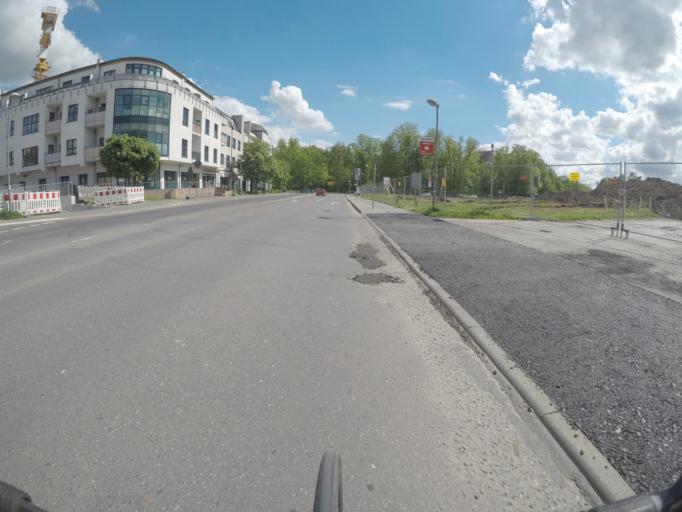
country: DE
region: Brandenburg
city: Bernau bei Berlin
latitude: 52.6829
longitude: 13.5853
